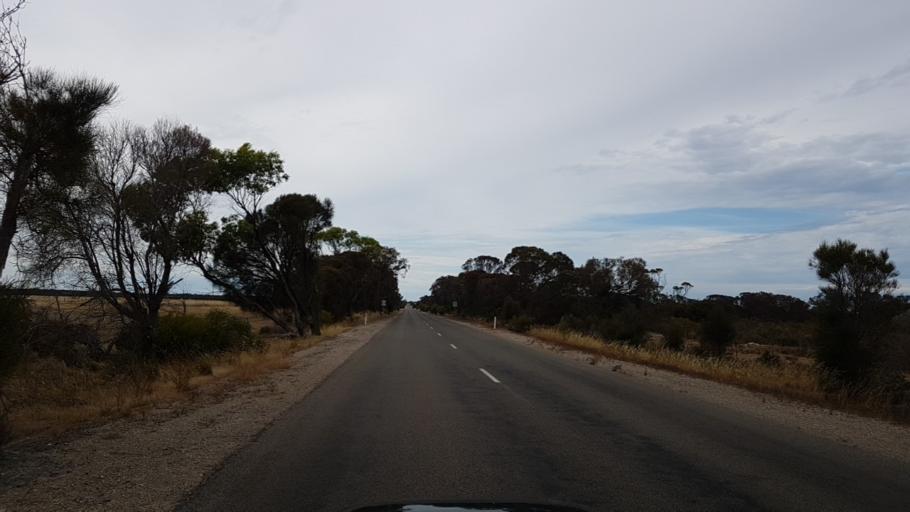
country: AU
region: South Australia
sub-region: Yorke Peninsula
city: Port Victoria
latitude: -34.9316
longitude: 137.0874
